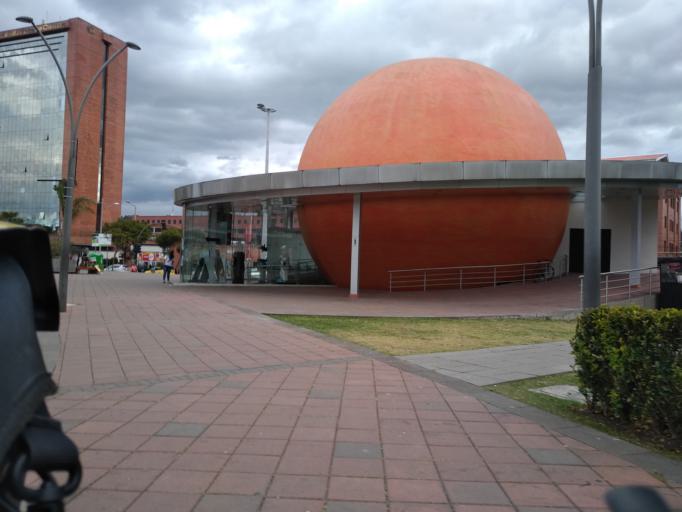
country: EC
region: Azuay
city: Cuenca
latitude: -2.9049
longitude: -79.0043
